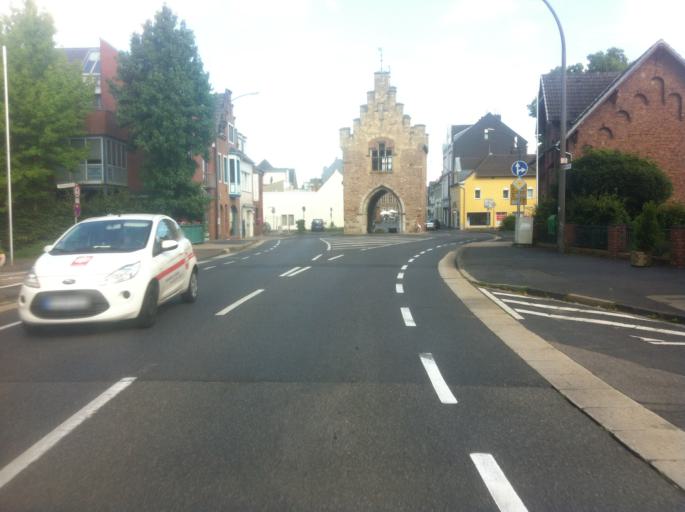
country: DE
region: North Rhine-Westphalia
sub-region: Regierungsbezirk Koln
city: Erftstadt
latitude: 50.8006
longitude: 6.7626
